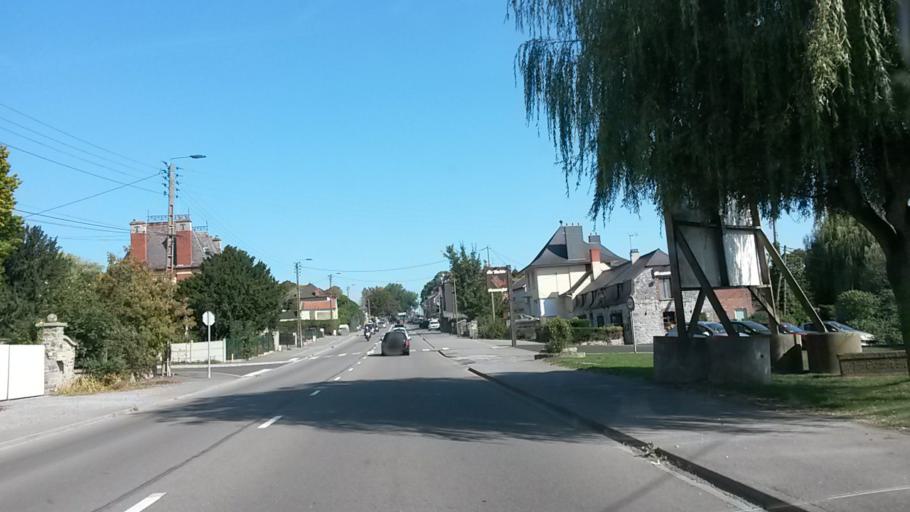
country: FR
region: Nord-Pas-de-Calais
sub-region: Departement du Nord
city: Avesnes-sur-Helpe
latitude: 50.1157
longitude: 3.9320
